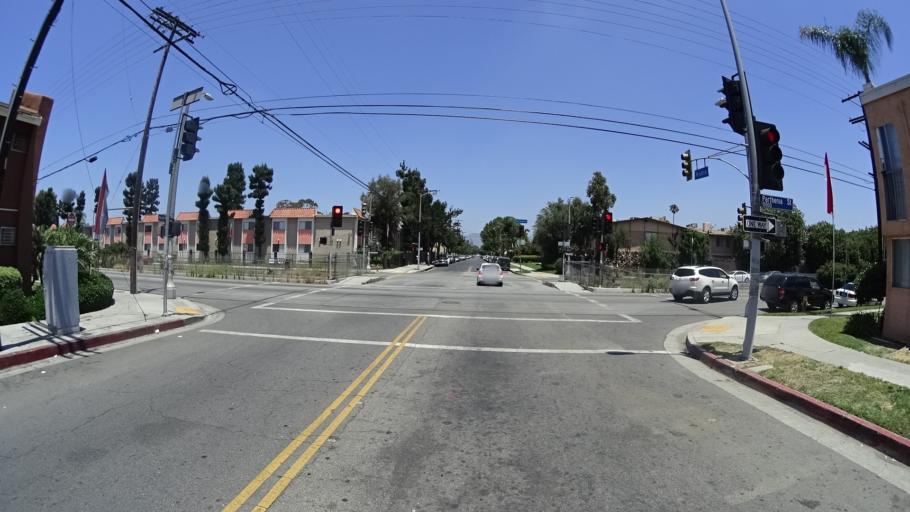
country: US
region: California
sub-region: Los Angeles County
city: Van Nuys
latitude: 34.2280
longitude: -118.4611
